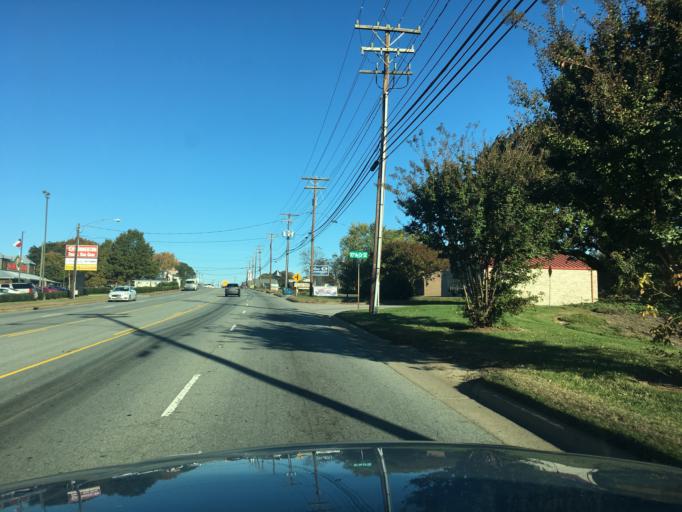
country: US
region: North Carolina
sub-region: Catawba County
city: Hickory
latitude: 35.7200
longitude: -81.3158
